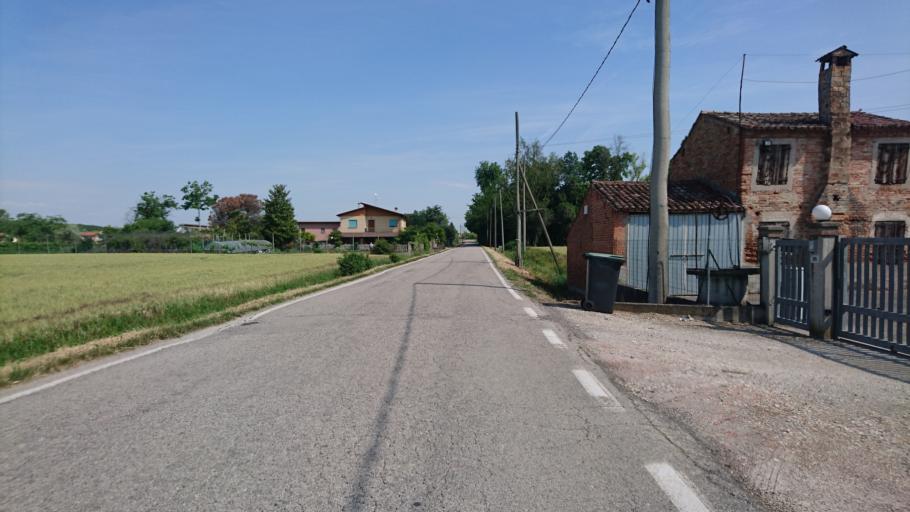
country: IT
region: Veneto
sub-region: Provincia di Padova
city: Megliadino San Vitale
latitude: 45.1909
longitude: 11.5030
